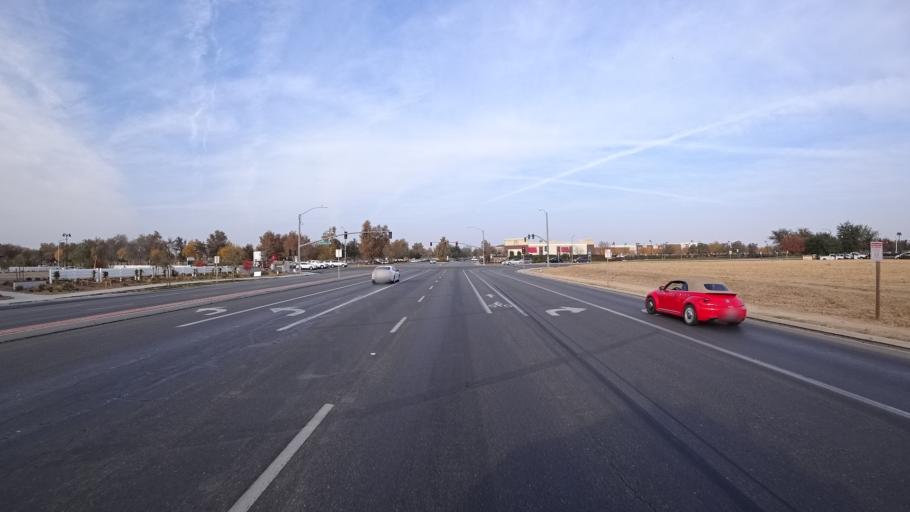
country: US
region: California
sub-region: Kern County
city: Greenacres
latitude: 35.3481
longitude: -119.1275
